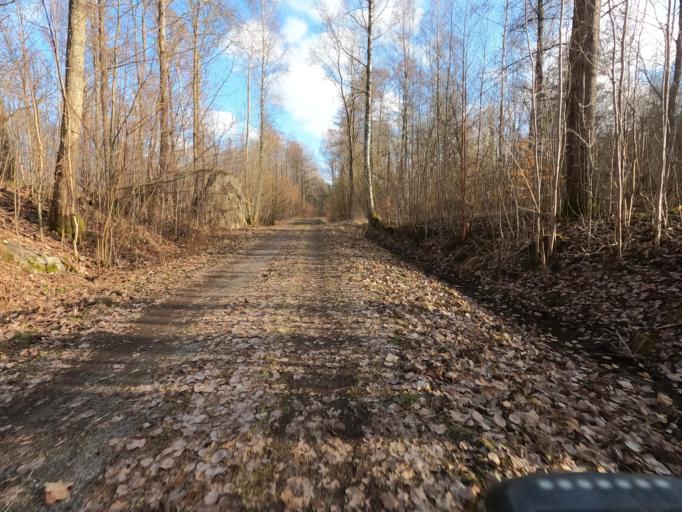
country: SE
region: Kronoberg
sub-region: Vaxjo Kommun
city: Gemla
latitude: 56.6792
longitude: 14.6129
